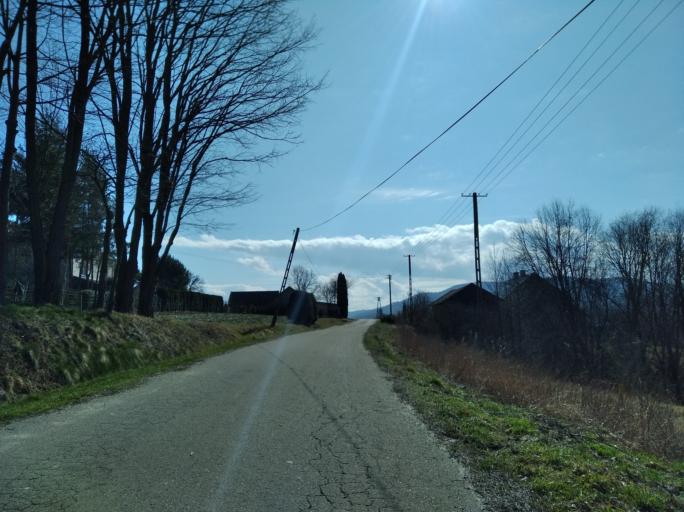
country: PL
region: Subcarpathian Voivodeship
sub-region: Powiat strzyzowski
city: Wysoka Strzyzowska
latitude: 49.8161
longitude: 21.7450
